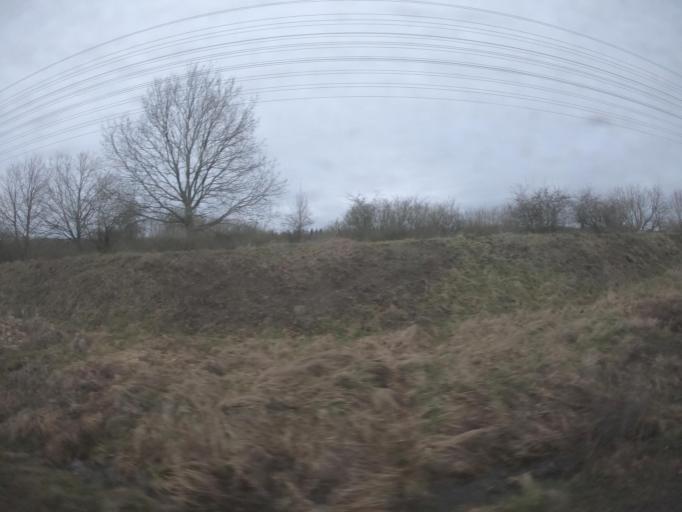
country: PL
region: West Pomeranian Voivodeship
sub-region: Powiat szczecinecki
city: Borne Sulinowo
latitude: 53.6553
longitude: 16.6055
